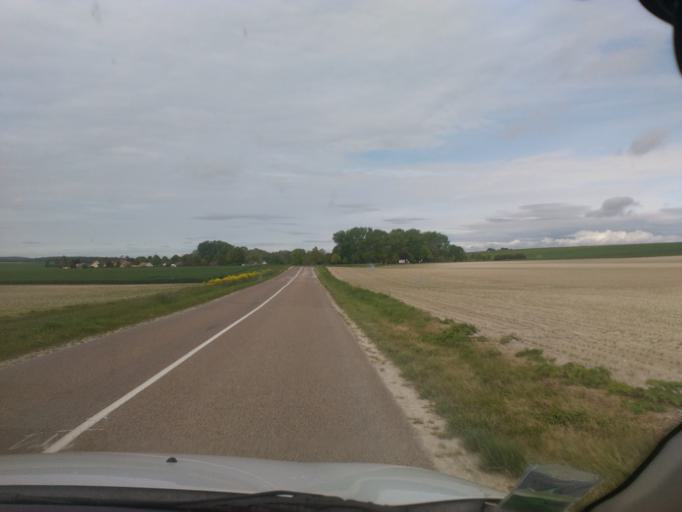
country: FR
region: Champagne-Ardenne
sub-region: Departement de l'Aube
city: Marigny-le-Chatel
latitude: 48.3623
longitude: 3.7174
